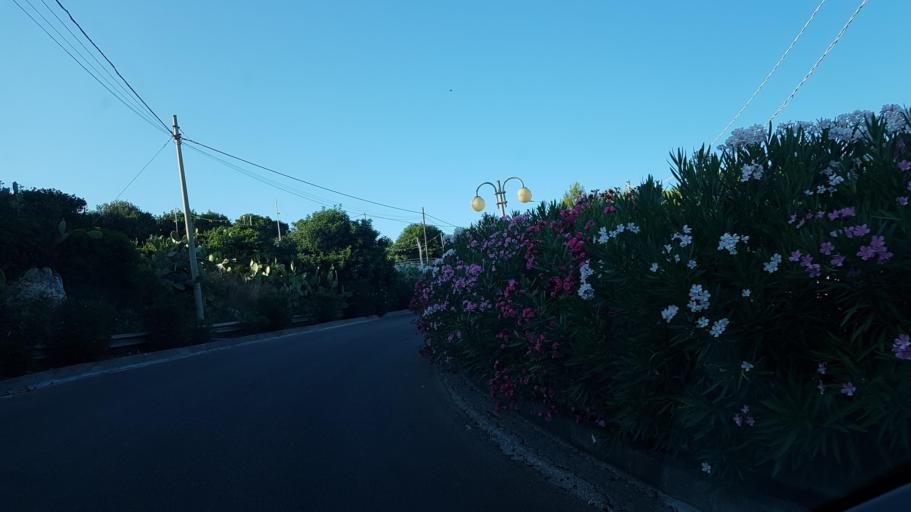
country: IT
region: Apulia
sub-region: Provincia di Lecce
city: Castro
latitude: 40.0017
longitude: 18.4225
